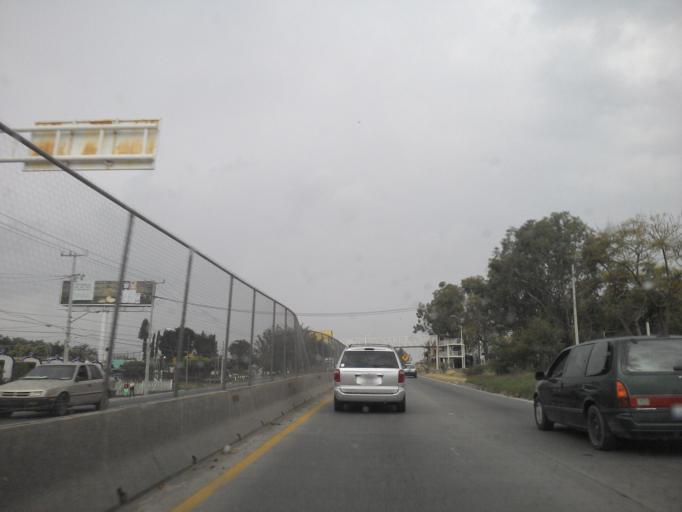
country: MX
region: Jalisco
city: Tlaquepaque
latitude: 20.6103
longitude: -103.2772
